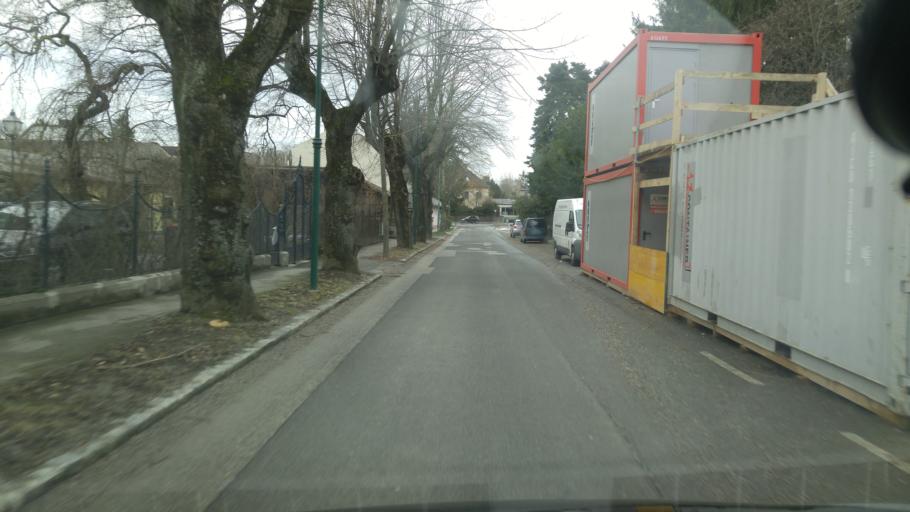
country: AT
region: Lower Austria
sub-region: Politischer Bezirk Baden
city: Bad Voslau
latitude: 47.9707
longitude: 16.2132
